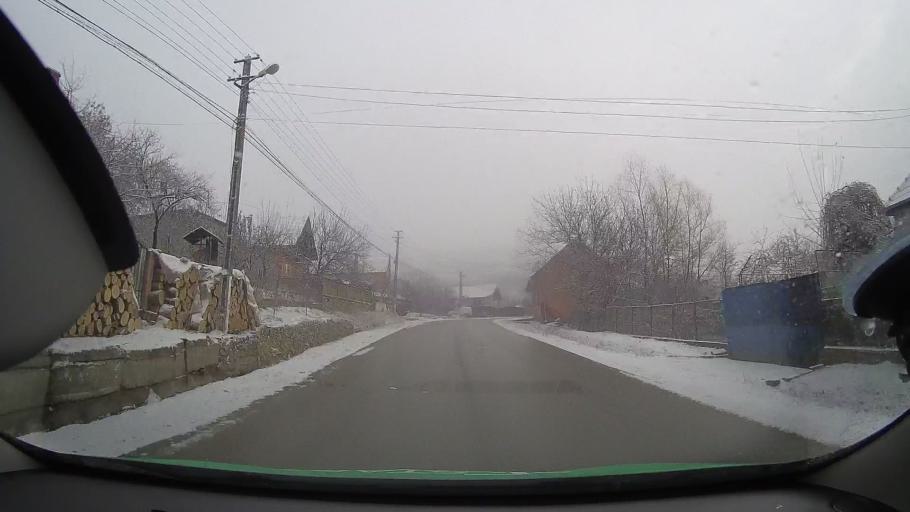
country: RO
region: Alba
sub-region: Municipiul Aiud
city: Ciumbrud
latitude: 46.3105
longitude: 23.7911
